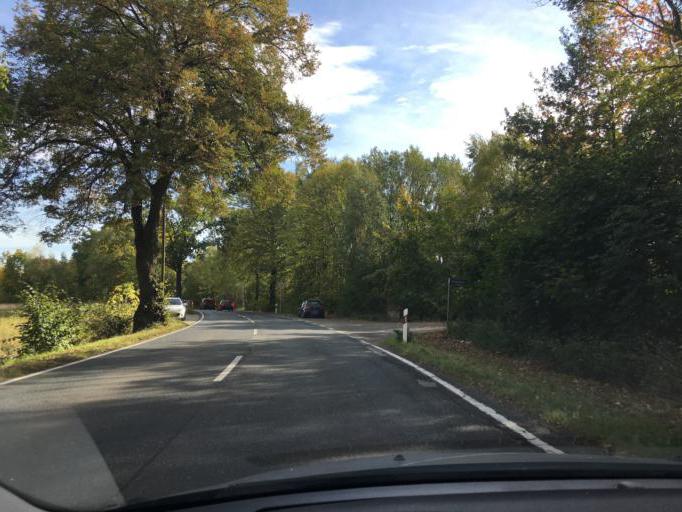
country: DE
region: Saxony
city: Wilsdruff
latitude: 51.0633
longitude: 13.5209
